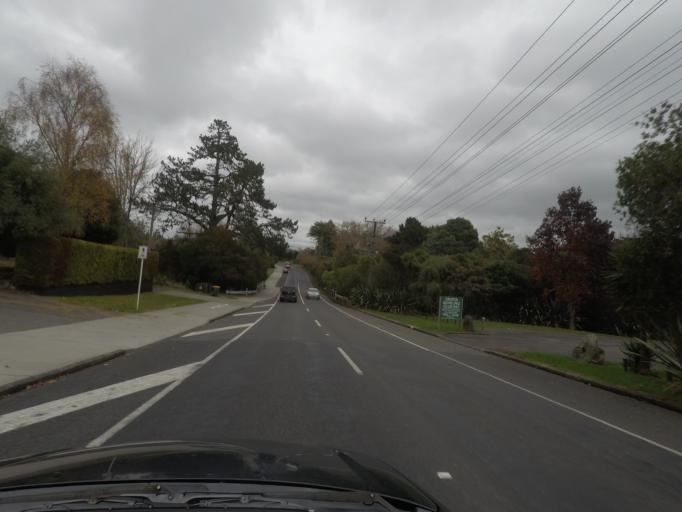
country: NZ
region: Auckland
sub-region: Auckland
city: Waitakere
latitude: -36.9097
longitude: 174.6243
